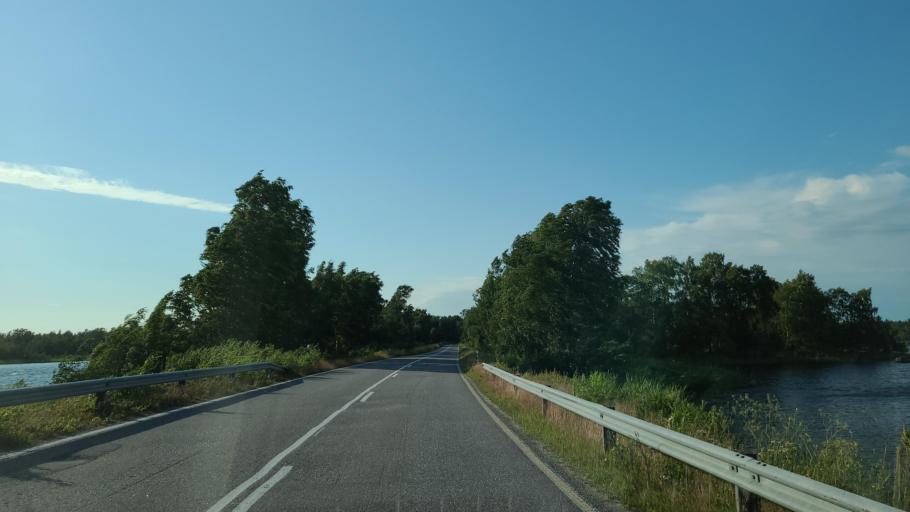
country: FI
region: Ostrobothnia
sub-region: Vaasa
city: Replot
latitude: 63.2824
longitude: 21.3367
